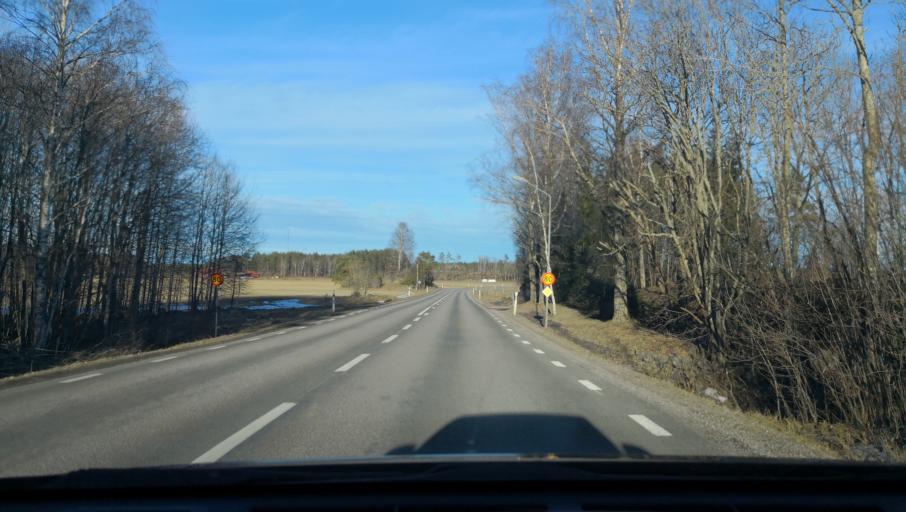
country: SE
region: Uppsala
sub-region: Osthammars Kommun
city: Gimo
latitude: 60.2173
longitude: 18.2126
